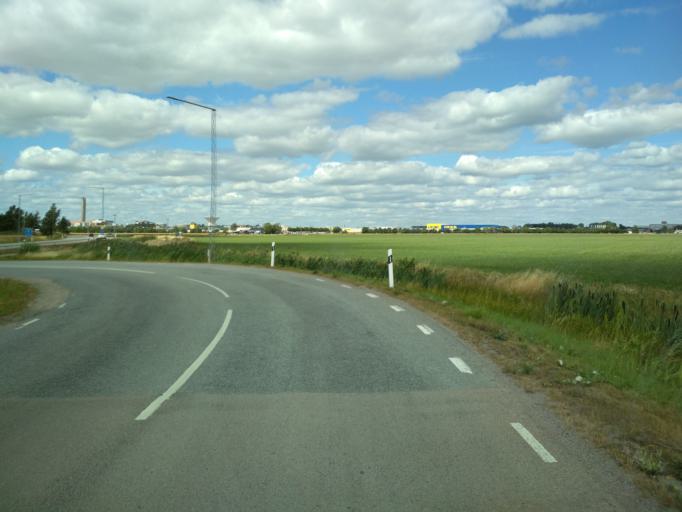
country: SE
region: Uppsala
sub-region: Uppsala Kommun
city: Saevja
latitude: 59.8360
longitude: 17.6924
